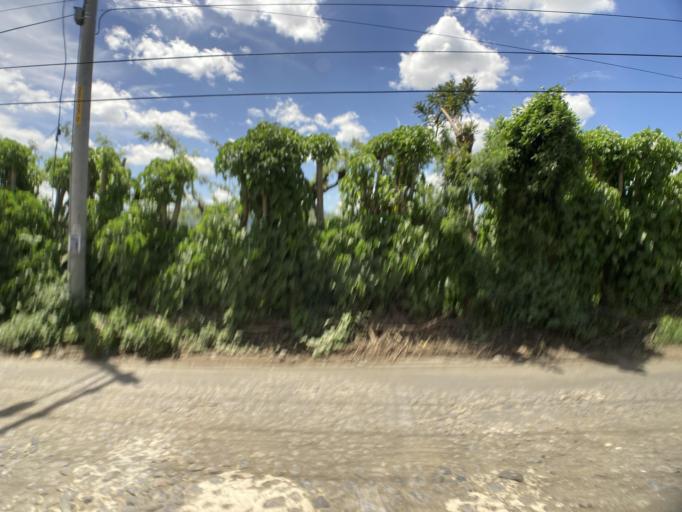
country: GT
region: Sacatepequez
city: Ciudad Vieja
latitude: 14.5278
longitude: -90.7456
